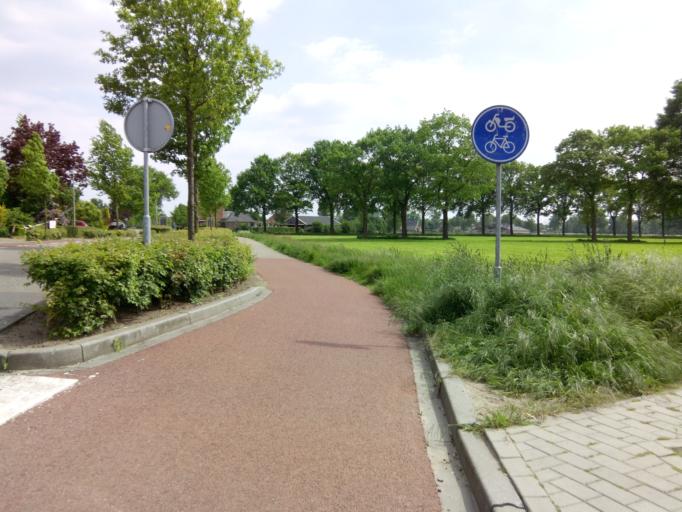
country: NL
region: Gelderland
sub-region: Berkelland
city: Borculo
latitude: 52.0642
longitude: 6.5664
